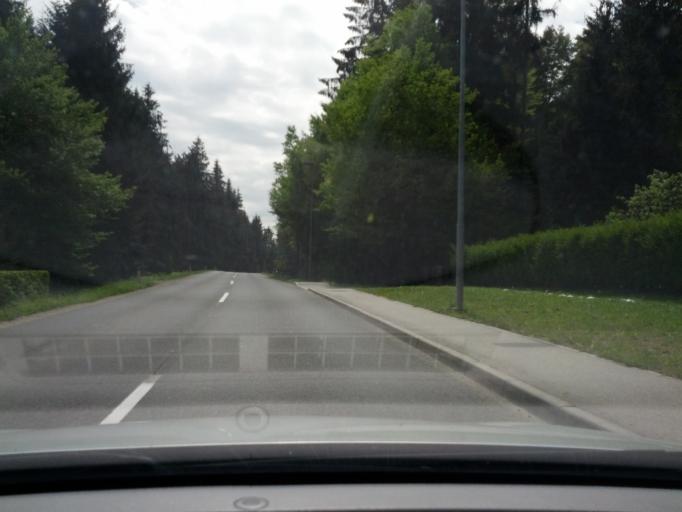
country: SI
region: Sentjur pri Celju
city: Sentjur
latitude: 46.2547
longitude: 15.3864
